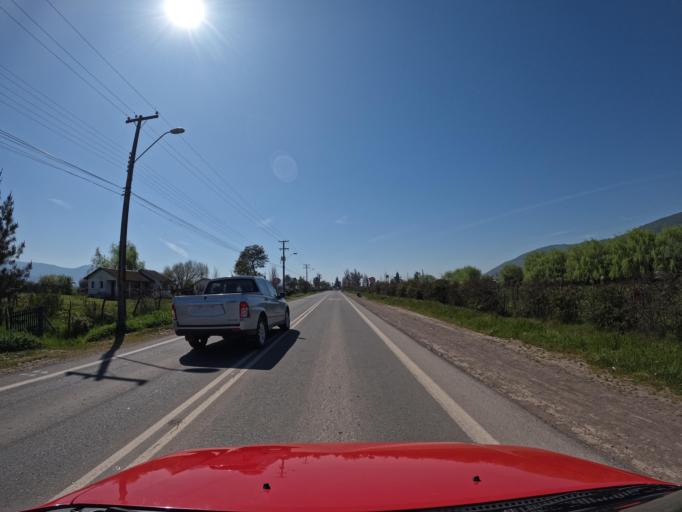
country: CL
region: Maule
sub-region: Provincia de Curico
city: Rauco
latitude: -35.0246
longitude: -71.4336
